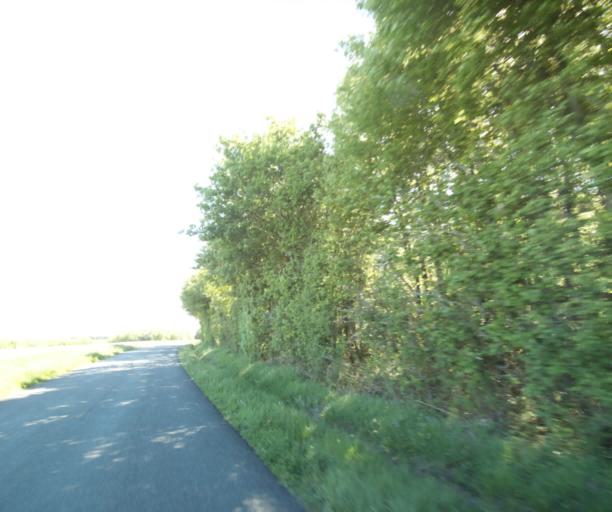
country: FR
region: Poitou-Charentes
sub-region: Departement de la Charente-Maritime
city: Bussac-sur-Charente
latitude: 45.8071
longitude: -0.6632
